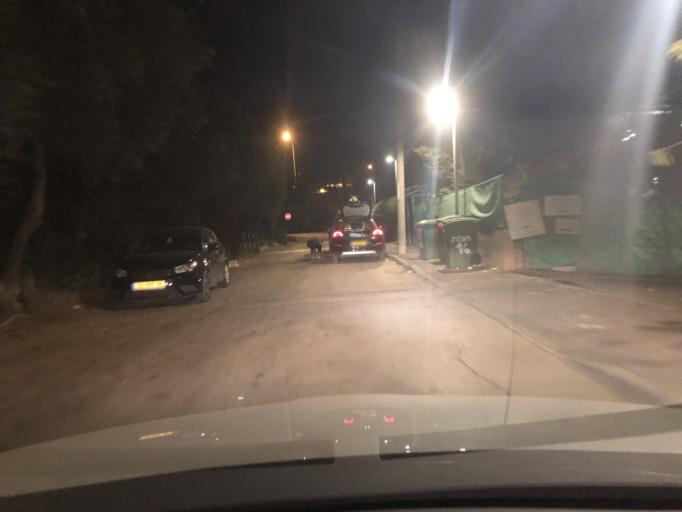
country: IL
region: Central District
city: Kfar Saba
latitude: 32.1709
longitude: 34.8960
